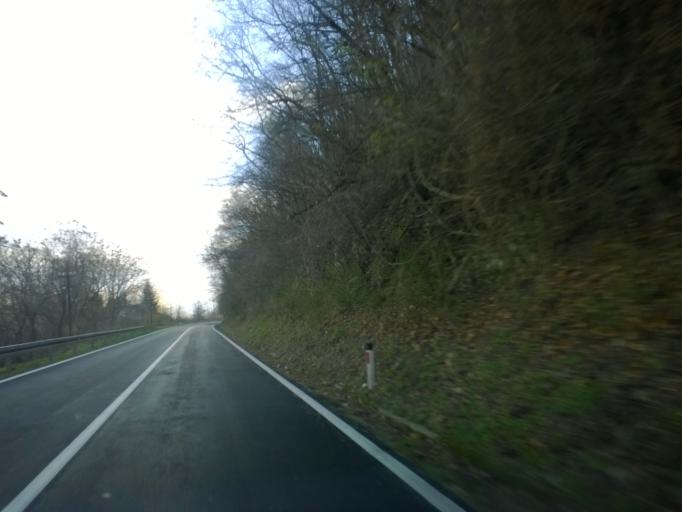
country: RS
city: Radenka
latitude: 44.6553
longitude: 21.7914
